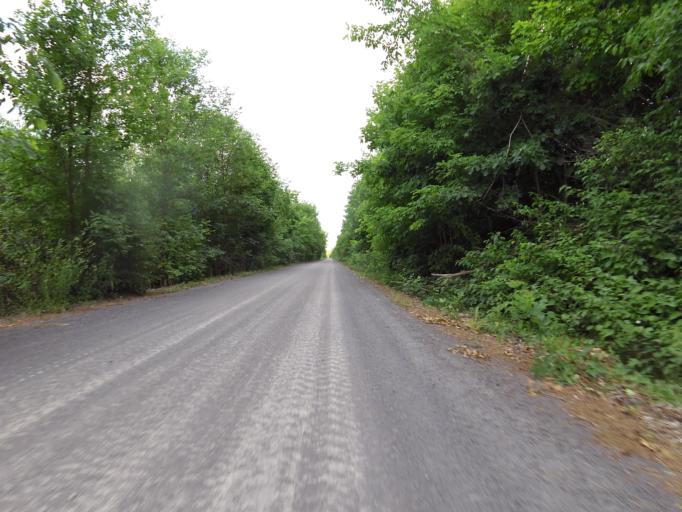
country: CA
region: Ontario
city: Arnprior
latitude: 45.3387
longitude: -76.2971
